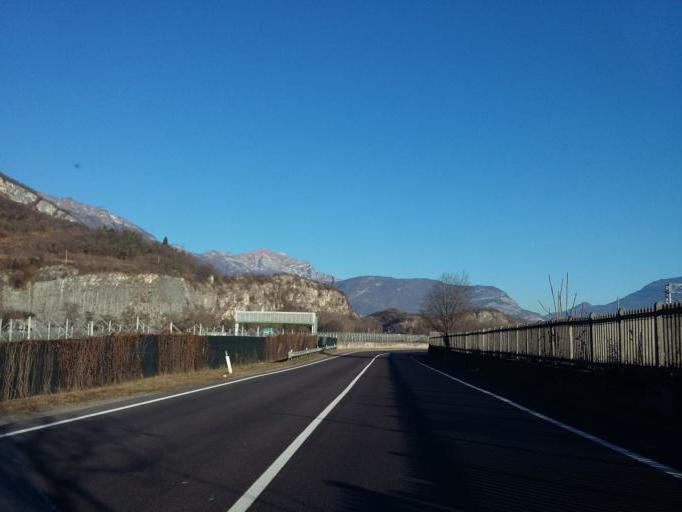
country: IT
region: Trentino-Alto Adige
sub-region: Provincia di Trento
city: Marco
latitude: 45.8628
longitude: 11.0027
